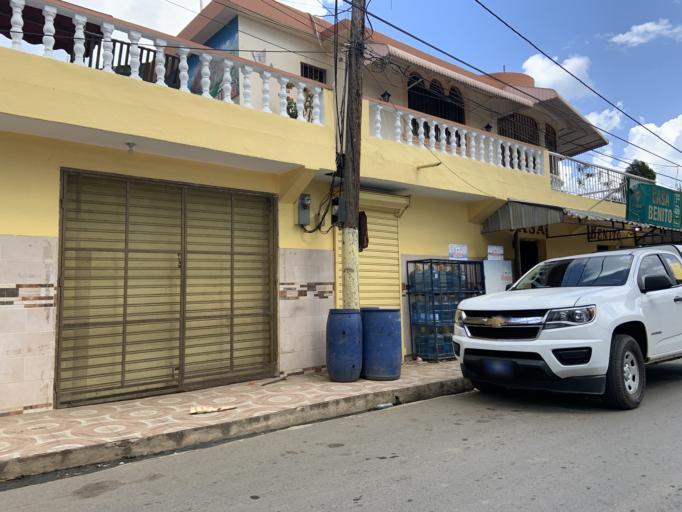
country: DO
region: Monte Plata
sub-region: Yamasa
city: Yamasa
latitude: 18.7713
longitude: -70.0190
